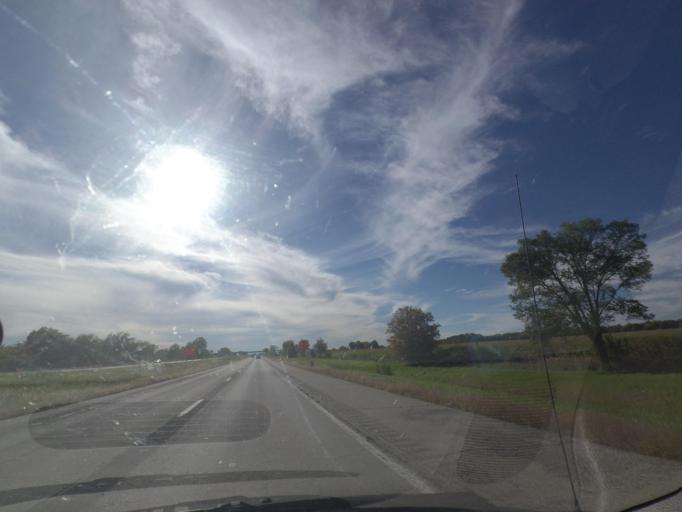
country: US
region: Illinois
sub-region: Macon County
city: Harristown
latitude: 39.8344
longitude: -89.0686
